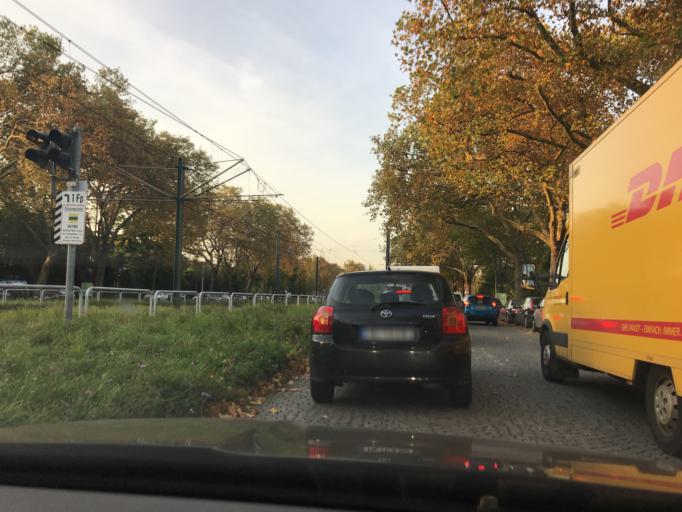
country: DE
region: North Rhine-Westphalia
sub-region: Regierungsbezirk Dusseldorf
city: Dusseldorf
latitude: 51.2626
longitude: 6.7538
